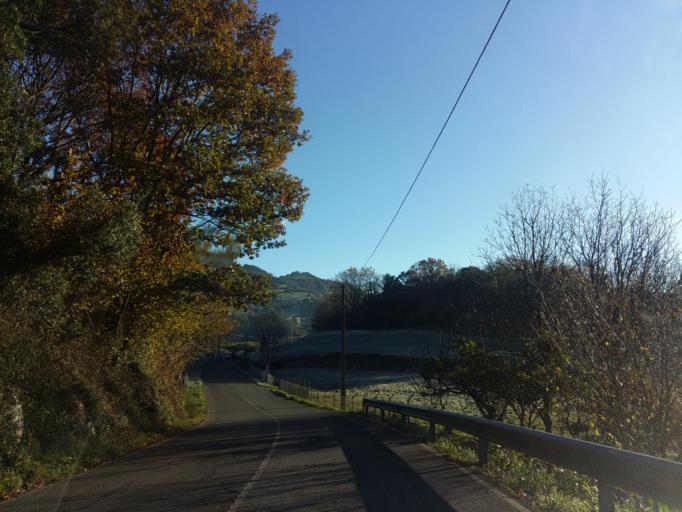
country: ES
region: Cantabria
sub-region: Provincia de Cantabria
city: Arredondo
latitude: 43.2807
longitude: -3.5356
